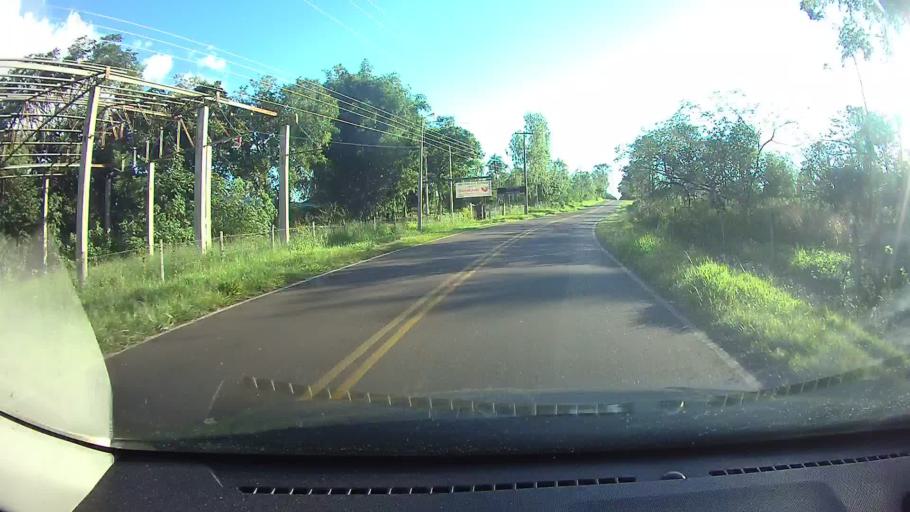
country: PY
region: Cordillera
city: Emboscada
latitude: -25.1981
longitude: -57.3200
